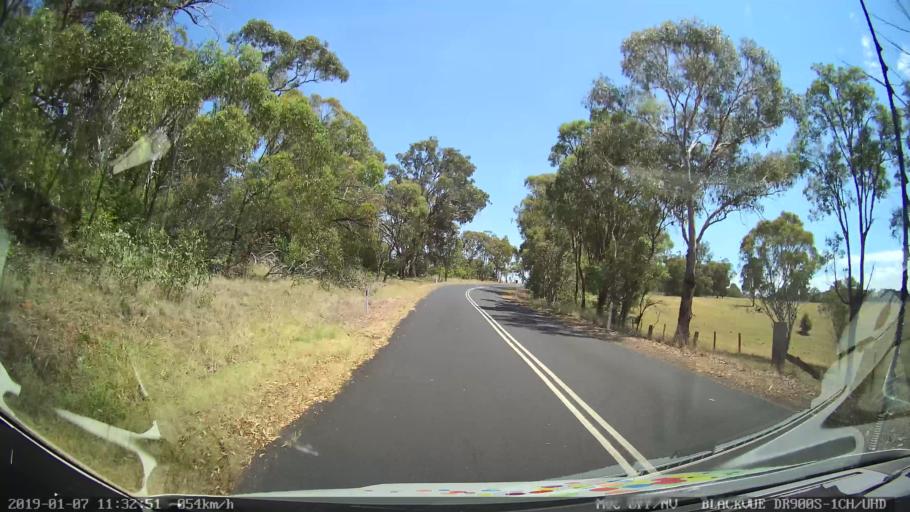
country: AU
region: New South Wales
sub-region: Armidale Dumaresq
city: Armidale
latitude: -30.4055
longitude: 151.5602
